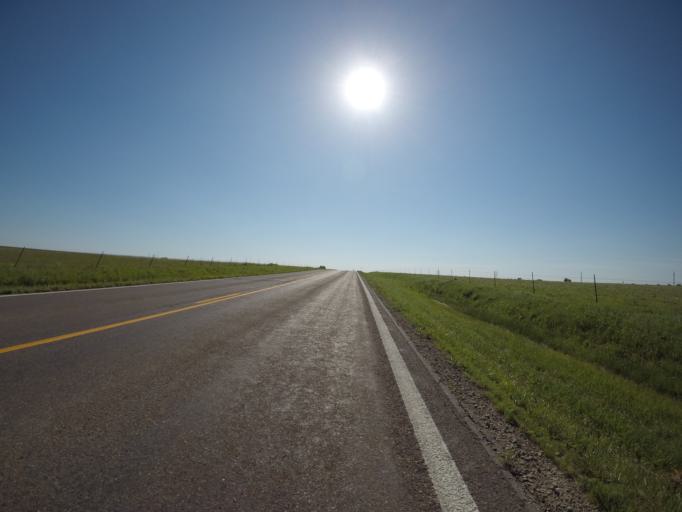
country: US
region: Kansas
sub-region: Lyon County
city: Emporia
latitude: 38.6516
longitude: -96.1150
